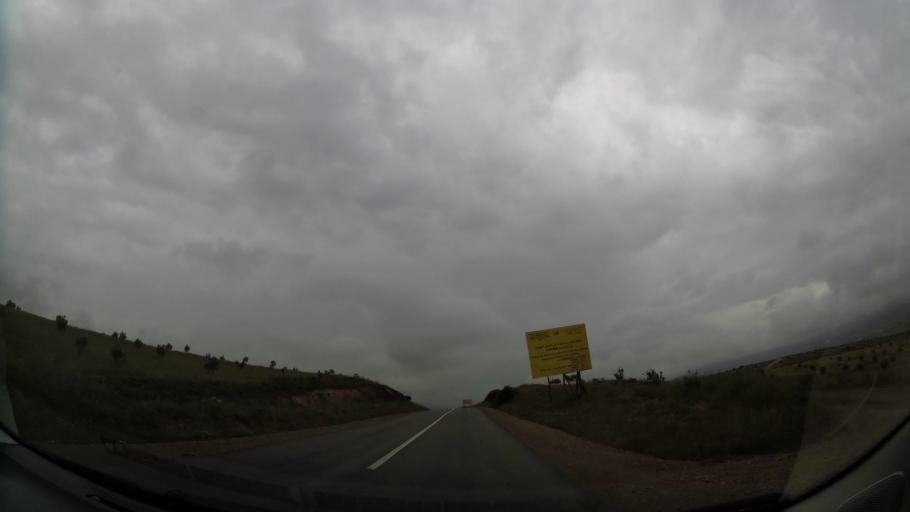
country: MA
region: Oriental
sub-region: Nador
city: Nador
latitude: 35.1527
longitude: -3.0368
